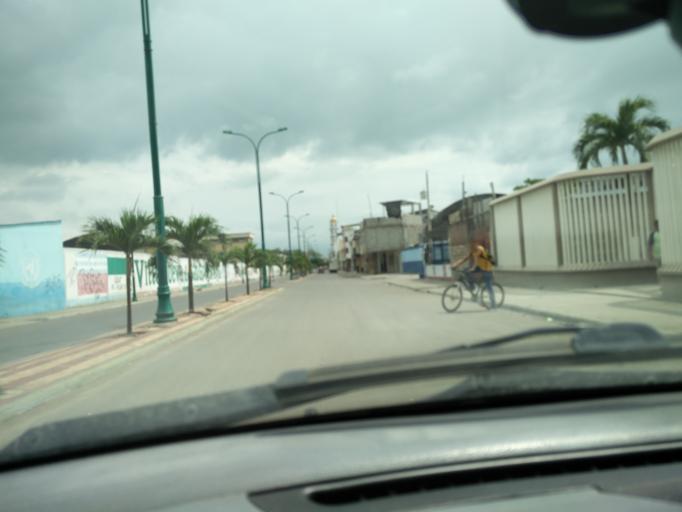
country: EC
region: Manabi
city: Portoviejo
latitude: -1.0507
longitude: -80.4509
